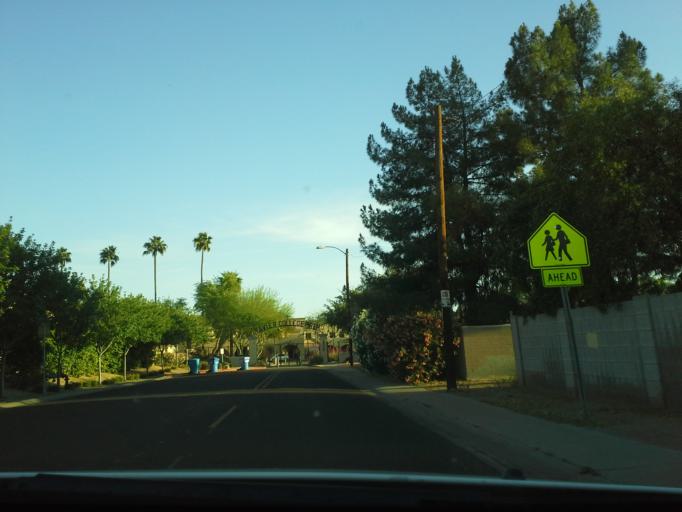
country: US
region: Arizona
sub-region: Maricopa County
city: Phoenix
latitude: 33.5066
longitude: -112.0672
